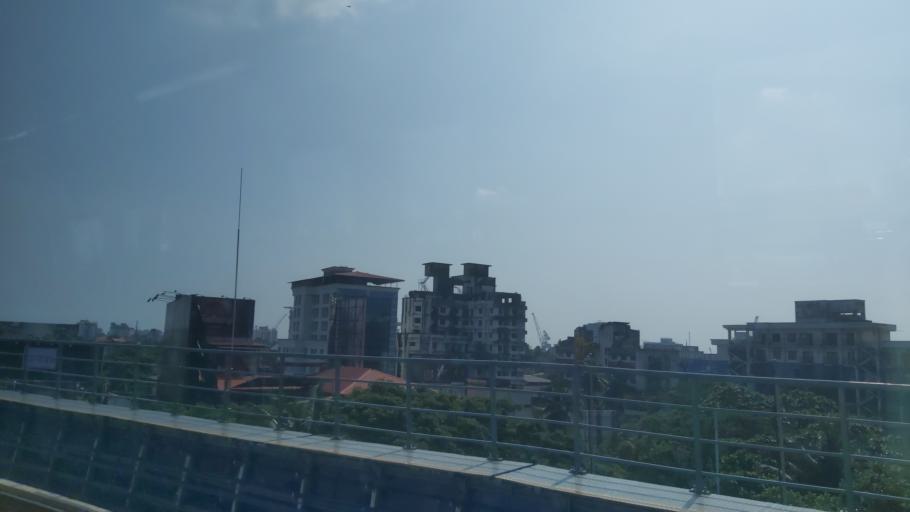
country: IN
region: Kerala
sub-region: Ernakulam
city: Cochin
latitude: 9.9661
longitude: 76.2919
